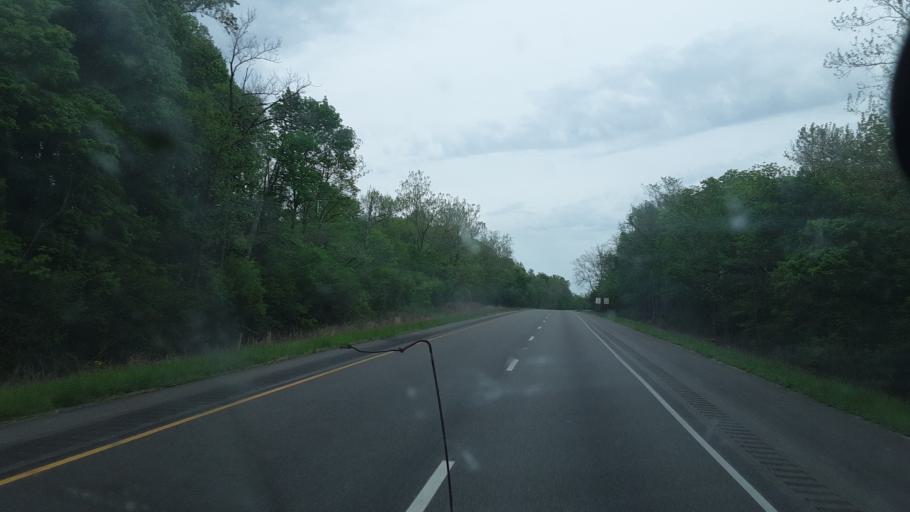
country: US
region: Indiana
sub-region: Posey County
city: Poseyville
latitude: 38.1937
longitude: -87.8459
